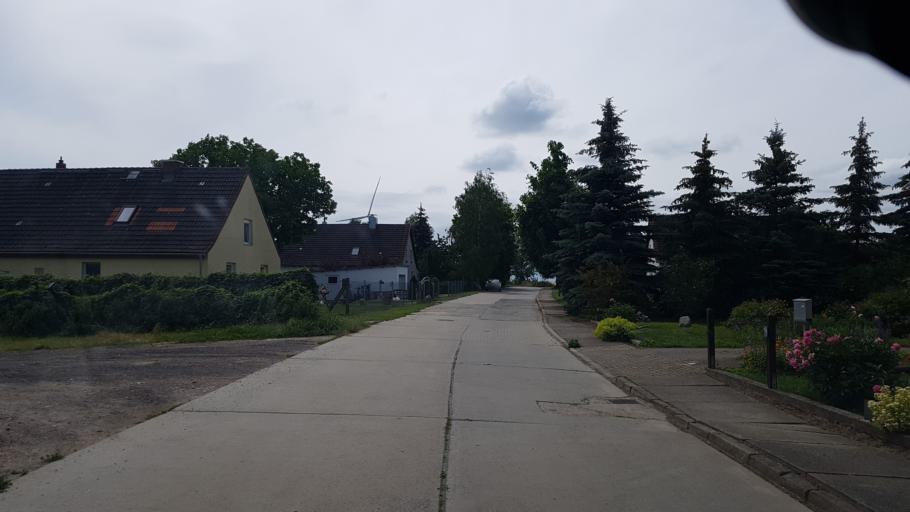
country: DE
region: Mecklenburg-Vorpommern
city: Strasburg
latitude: 53.4475
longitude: 13.8078
